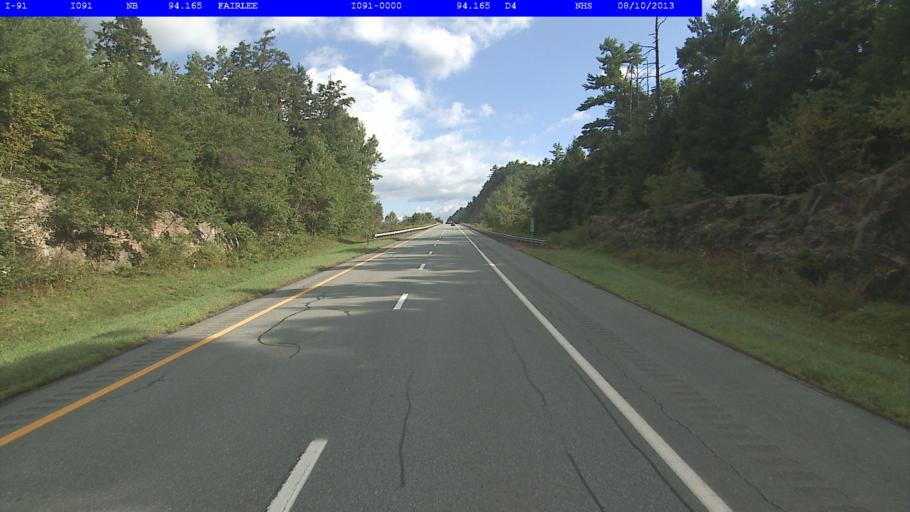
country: US
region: New Hampshire
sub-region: Grafton County
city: Orford
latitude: 43.9354
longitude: -72.1334
